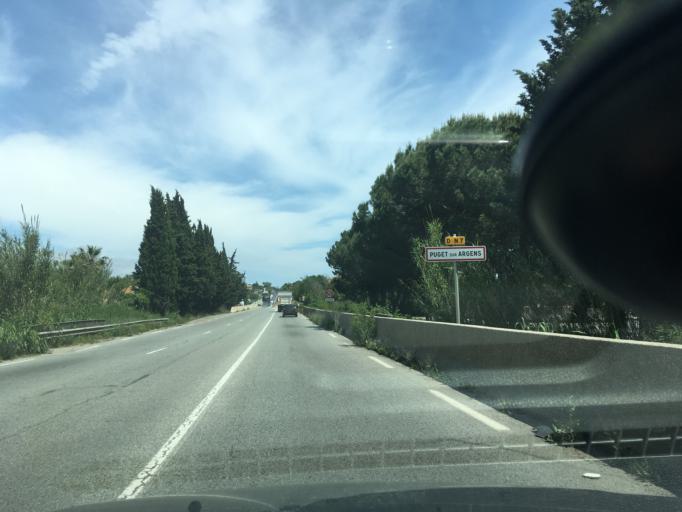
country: FR
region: Provence-Alpes-Cote d'Azur
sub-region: Departement du Var
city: Puget-sur-Argens
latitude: 43.4582
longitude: 6.6758
